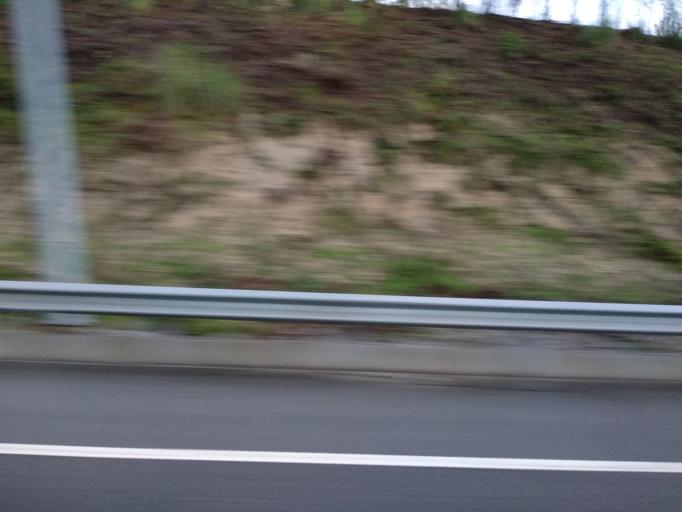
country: PT
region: Braga
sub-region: Vila Nova de Famalicao
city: Vila Nova de Famalicao
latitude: 41.3913
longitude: -8.5176
